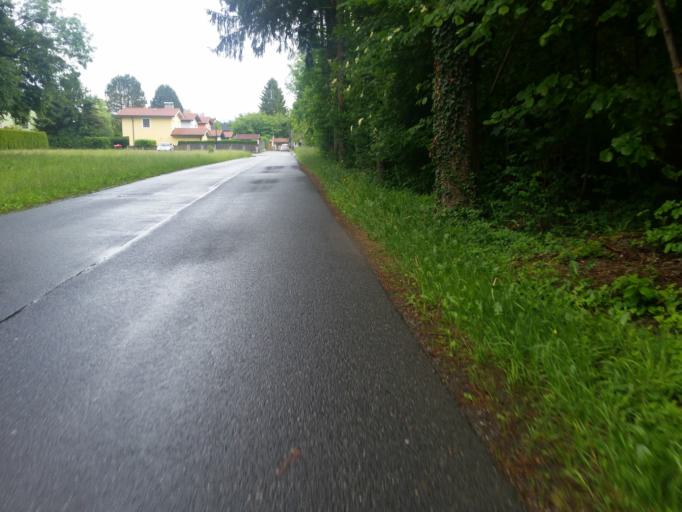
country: AT
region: Salzburg
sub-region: Salzburg Stadt
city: Salzburg
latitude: 47.7827
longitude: 13.0007
